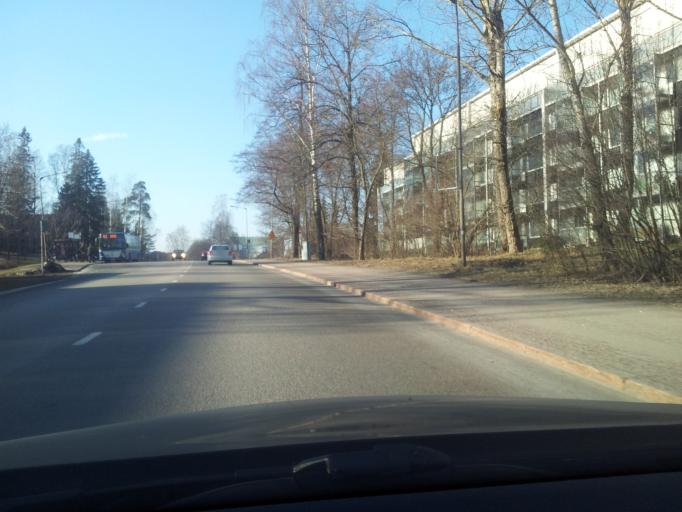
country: FI
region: Uusimaa
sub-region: Helsinki
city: Otaniemi
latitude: 60.1823
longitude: 24.8331
